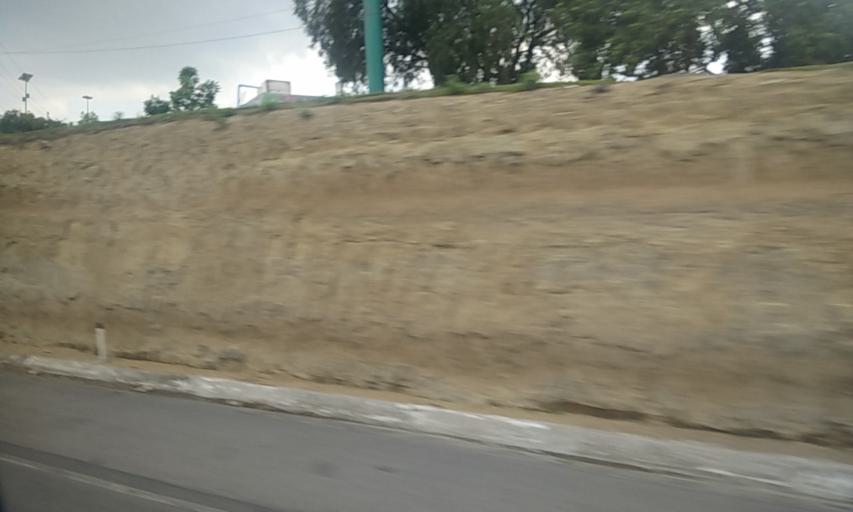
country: MX
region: Mexico
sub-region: Tepotzotlan
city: Santa Cruz del Monte
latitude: 19.7511
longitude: -99.2137
